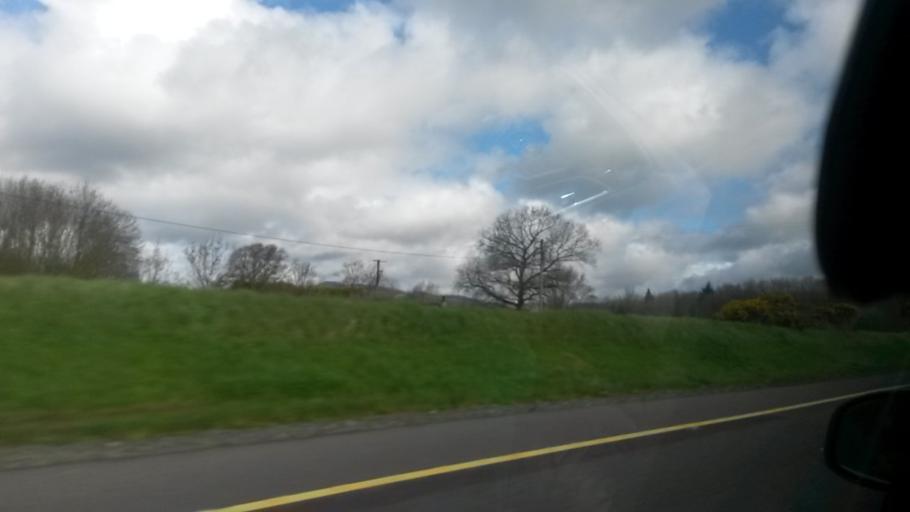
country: IE
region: Munster
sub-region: County Cork
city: Mitchelstown
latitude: 52.2701
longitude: -8.2409
